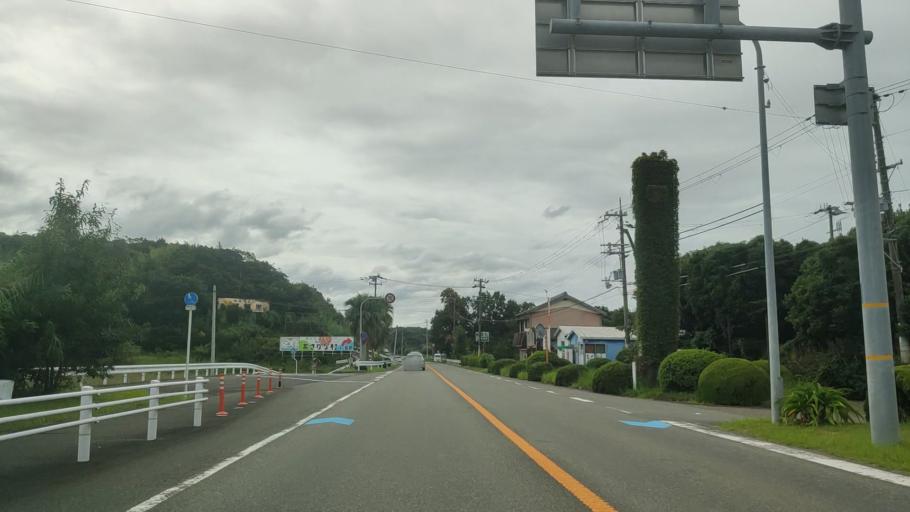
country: JP
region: Wakayama
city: Tanabe
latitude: 33.6987
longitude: 135.3886
